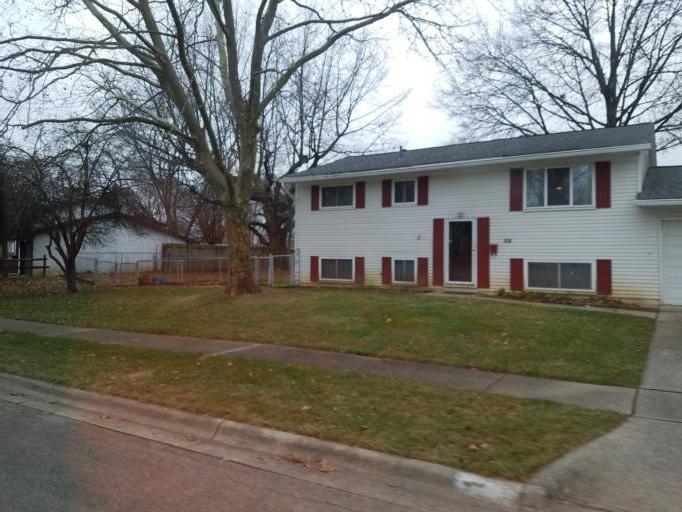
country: US
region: Ohio
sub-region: Franklin County
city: Worthington
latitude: 40.1019
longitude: -82.9777
